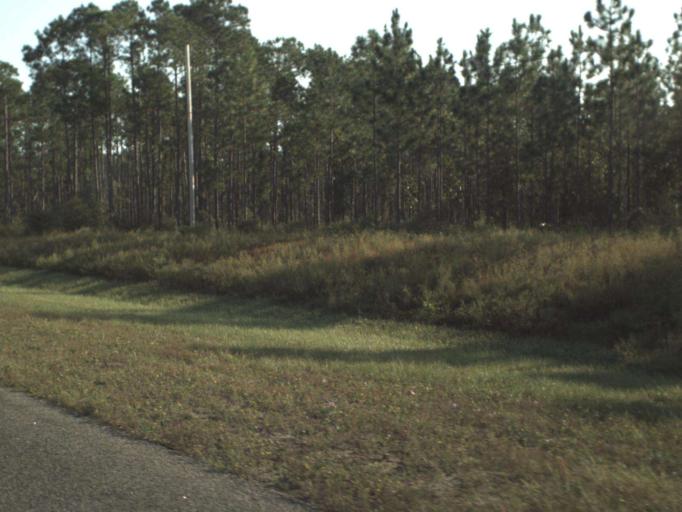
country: US
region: Florida
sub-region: Bay County
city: Laguna Beach
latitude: 30.4038
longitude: -85.8706
